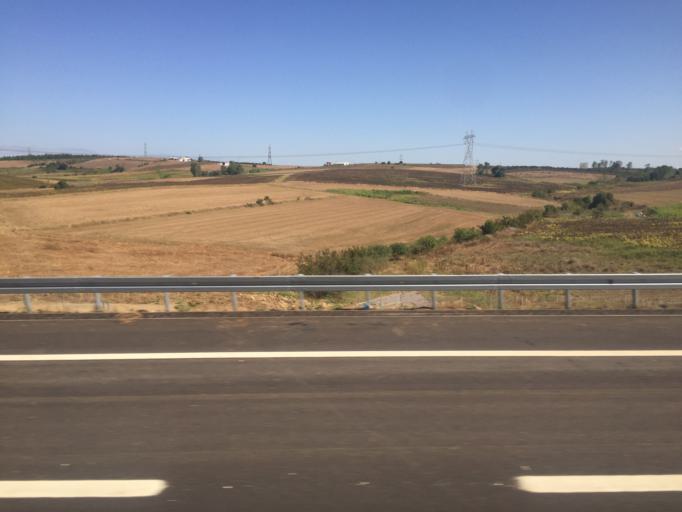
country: TR
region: Bursa
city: Mahmudiye
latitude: 40.2735
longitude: 28.5946
